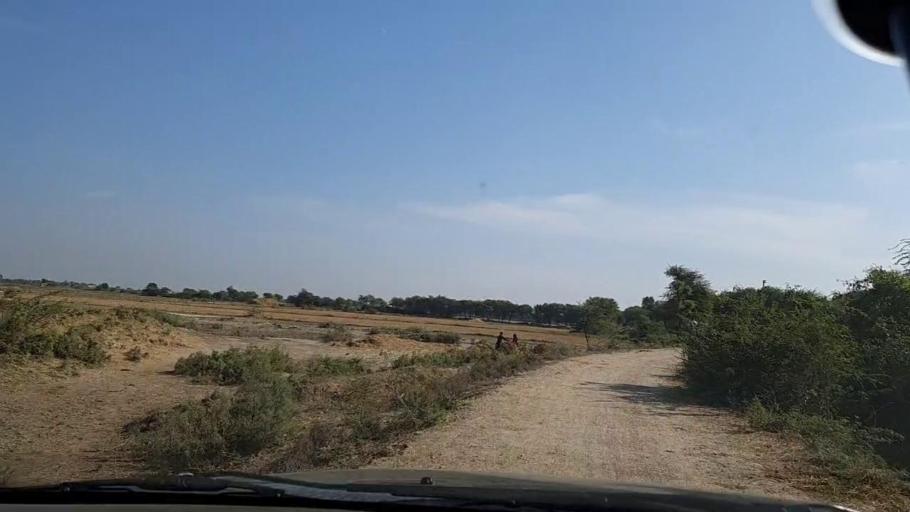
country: PK
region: Sindh
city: Mirpur Batoro
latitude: 24.6327
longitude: 68.2630
